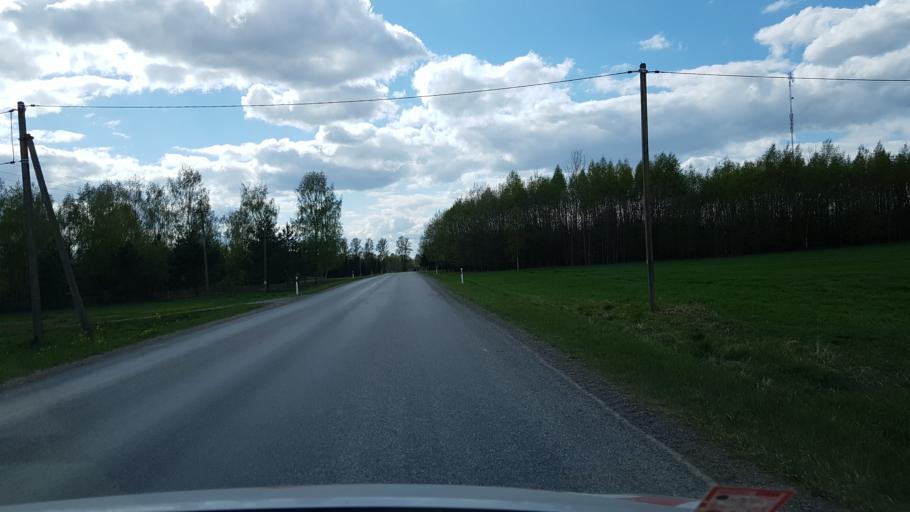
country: EE
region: Polvamaa
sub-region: Polva linn
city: Polva
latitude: 58.2828
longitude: 27.0118
